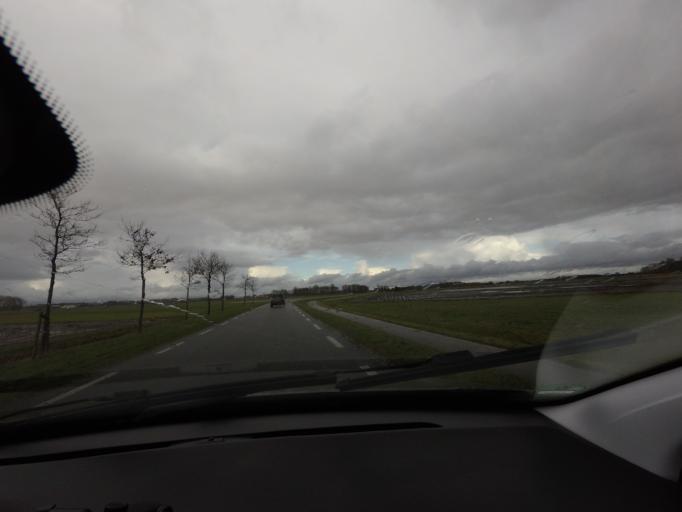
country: NL
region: Groningen
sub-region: Gemeente Veendam
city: Veendam
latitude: 53.0335
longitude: 6.8096
